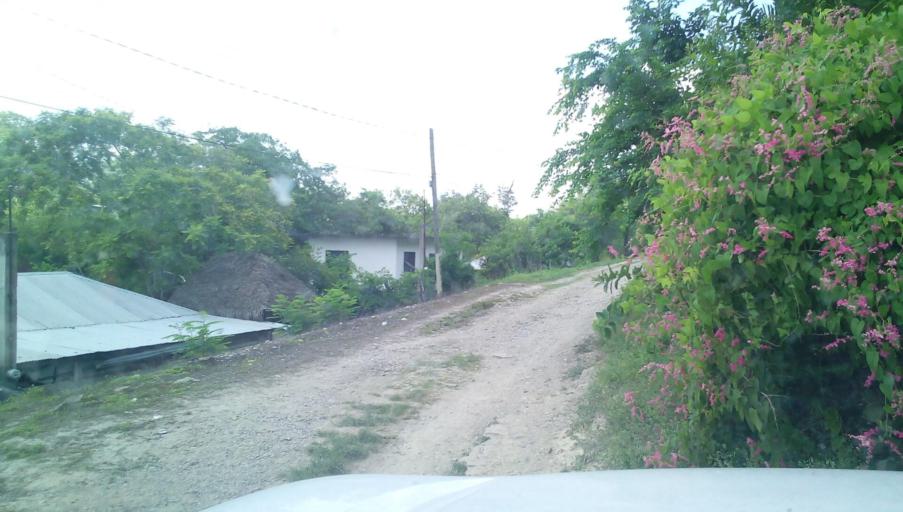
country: MX
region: Veracruz
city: Tempoal de Sanchez
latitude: 21.6058
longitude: -98.2879
